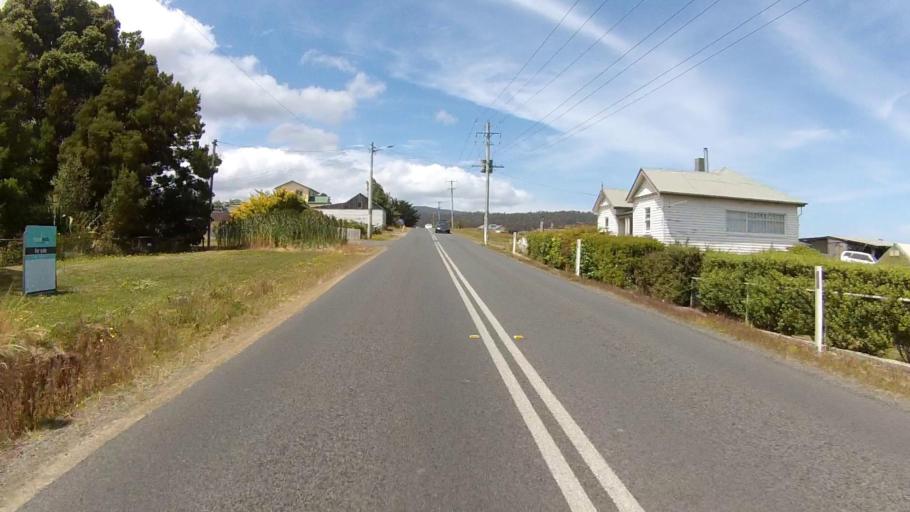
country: AU
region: Tasmania
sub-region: Huon Valley
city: Cygnet
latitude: -43.1645
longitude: 147.0869
